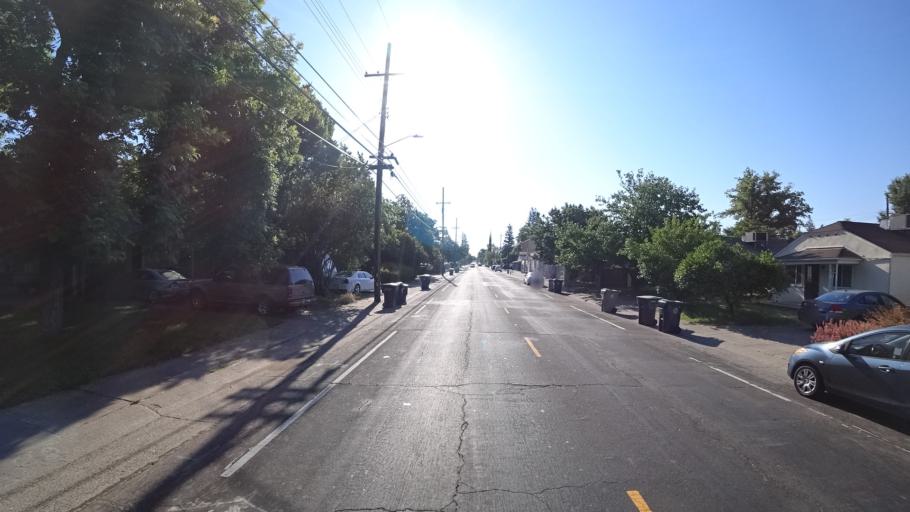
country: US
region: California
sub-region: Sacramento County
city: Parkway
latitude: 38.5395
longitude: -121.4431
